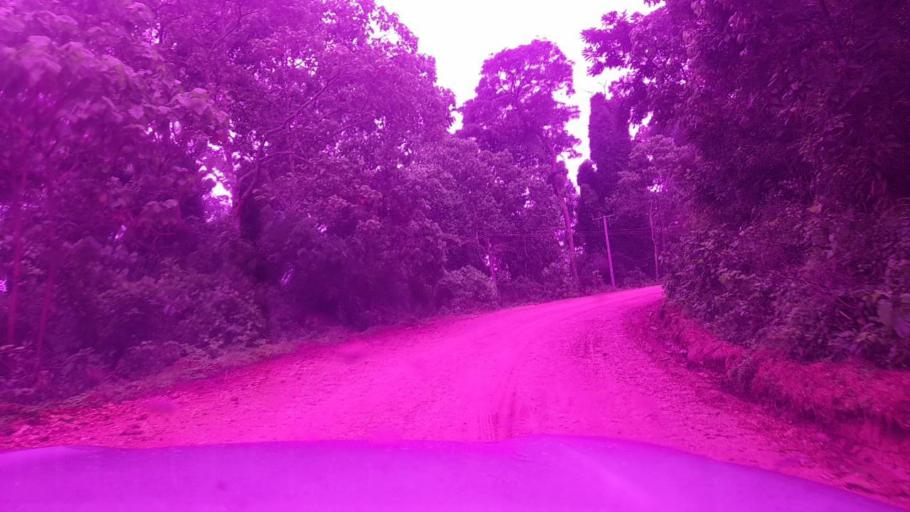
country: ET
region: Southern Nations, Nationalities, and People's Region
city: Bonga
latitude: 7.5042
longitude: 36.1010
